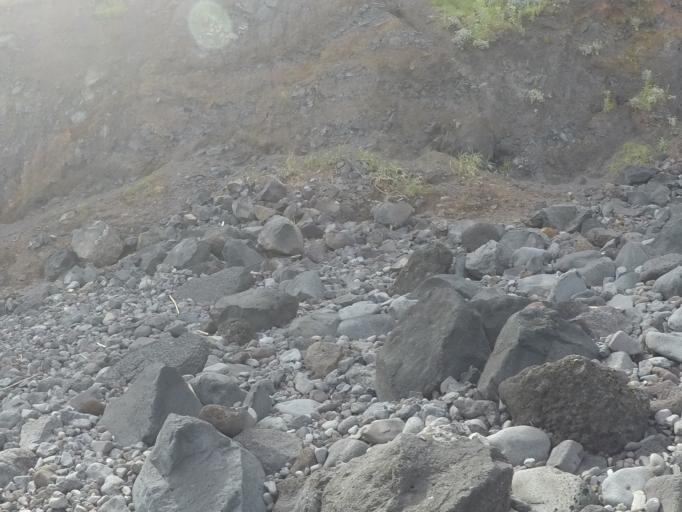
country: PT
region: Madeira
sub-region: Sao Vicente
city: Sao Vicente
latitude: 32.8278
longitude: -16.9963
